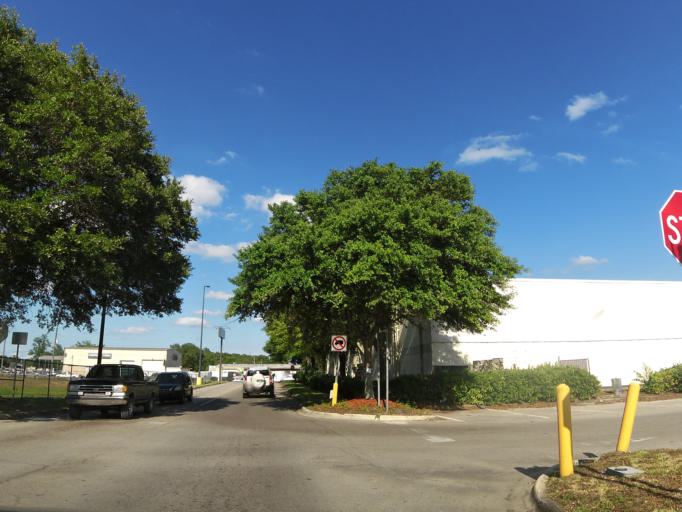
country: US
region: Florida
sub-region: Putnam County
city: Palatka
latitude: 29.6380
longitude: -81.6800
